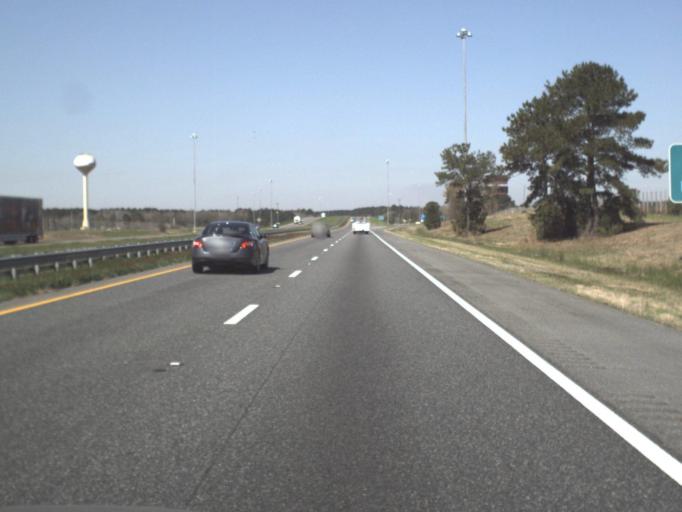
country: US
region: Florida
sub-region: Jackson County
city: Marianna
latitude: 30.7500
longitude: -85.2654
